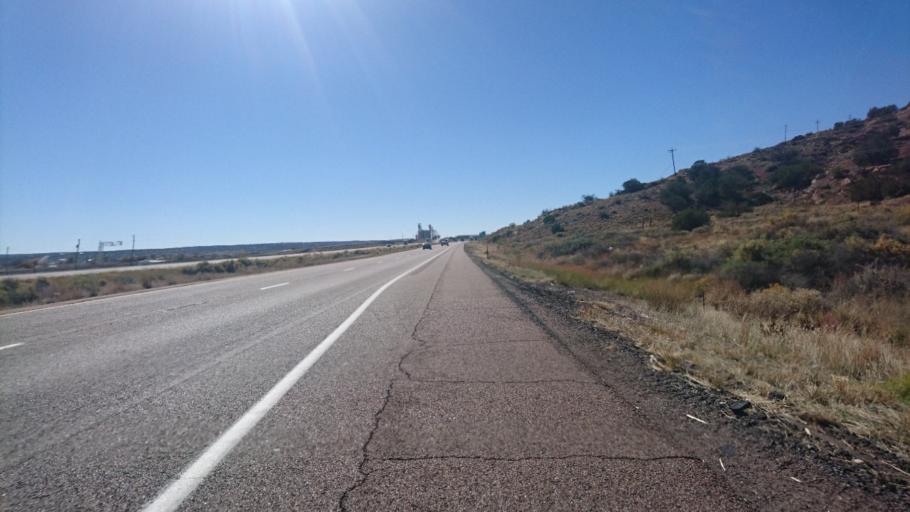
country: US
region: Arizona
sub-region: Apache County
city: Houck
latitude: 35.2211
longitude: -109.3250
